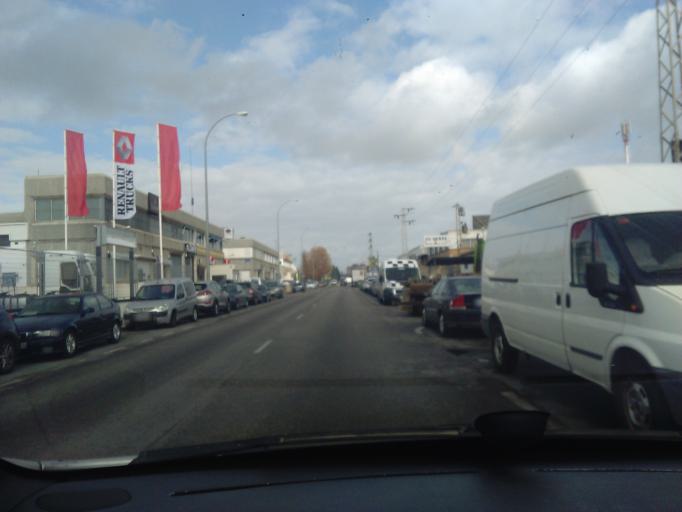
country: ES
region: Andalusia
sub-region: Provincia de Sevilla
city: Sevilla
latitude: 37.3753
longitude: -5.9271
